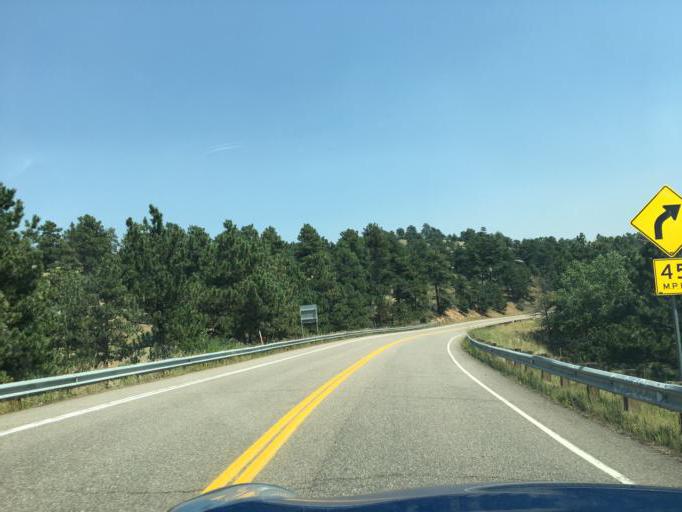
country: US
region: Colorado
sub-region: Jefferson County
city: Genesee
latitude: 39.7115
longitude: -105.2706
